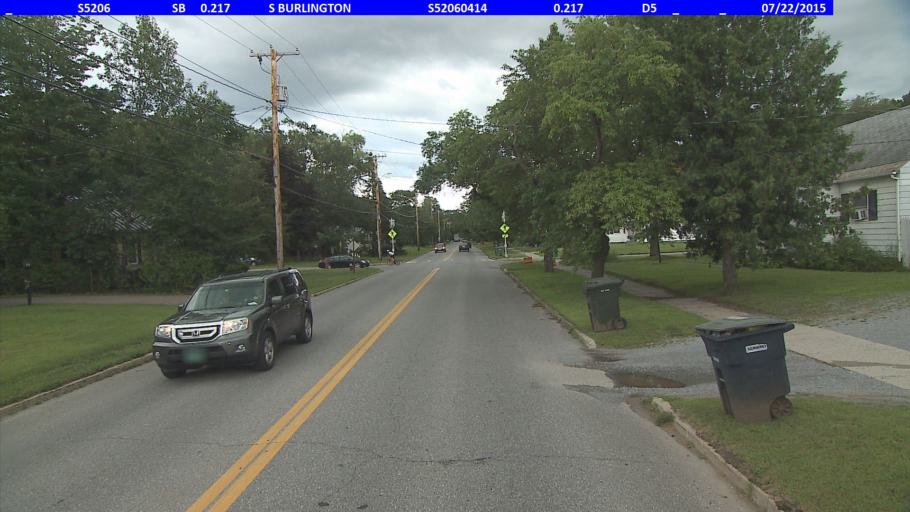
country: US
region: Vermont
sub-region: Chittenden County
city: South Burlington
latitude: 44.4737
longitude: -73.1646
